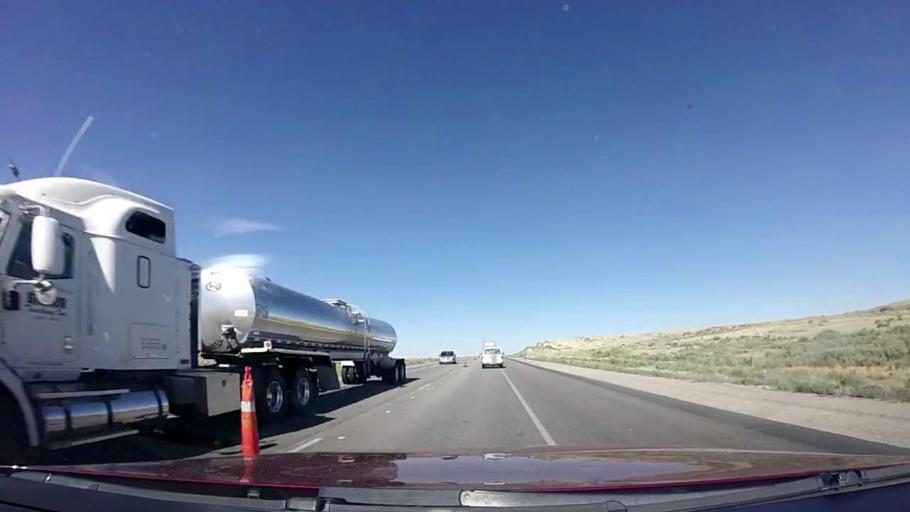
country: US
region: Wyoming
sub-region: Carbon County
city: Rawlins
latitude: 41.7065
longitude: -107.8646
